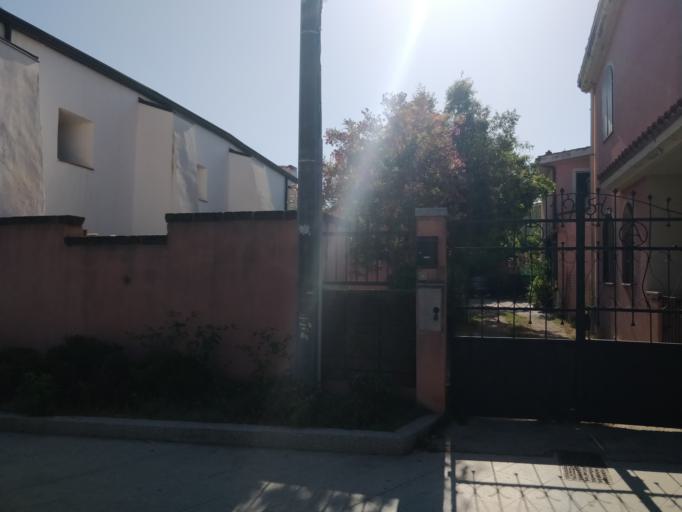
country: IT
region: Sardinia
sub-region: Provincia di Ogliastra
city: Girasole
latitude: 39.9527
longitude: 9.6639
